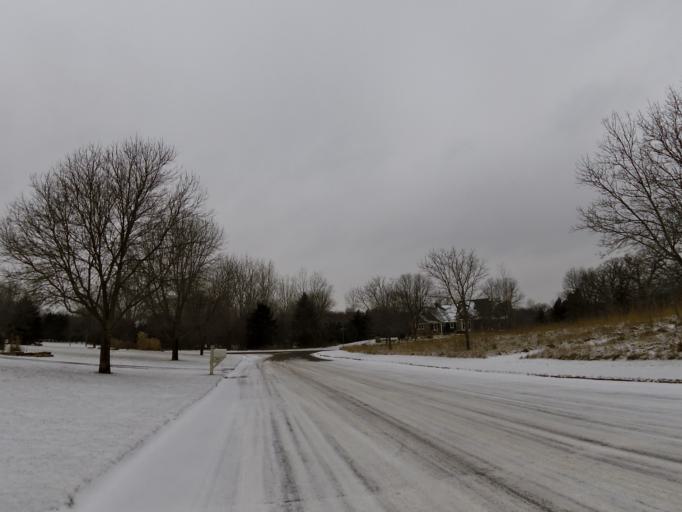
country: US
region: Minnesota
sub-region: Washington County
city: Lakeland
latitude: 44.9611
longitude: -92.8221
